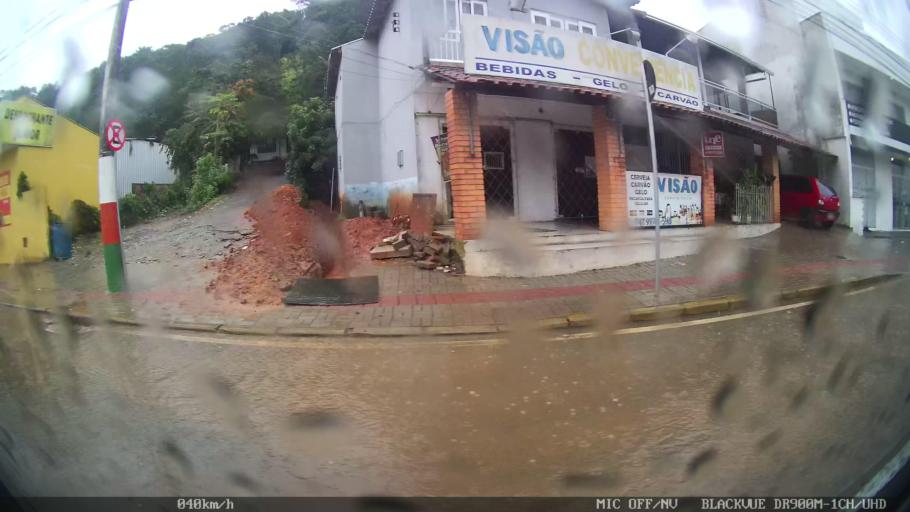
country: BR
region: Santa Catarina
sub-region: Balneario Camboriu
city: Balneario Camboriu
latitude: -27.0086
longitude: -48.6490
